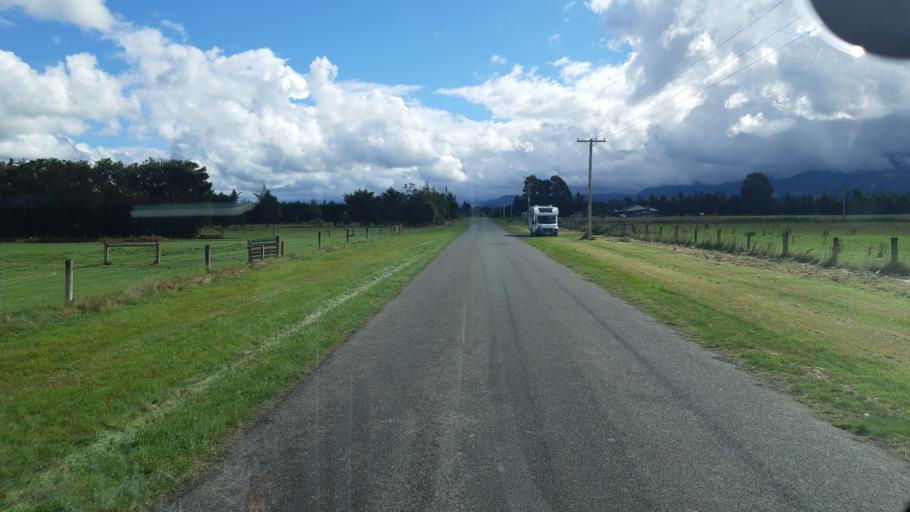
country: NZ
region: Canterbury
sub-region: Waimakariri District
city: Oxford
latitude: -43.3130
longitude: 172.1646
